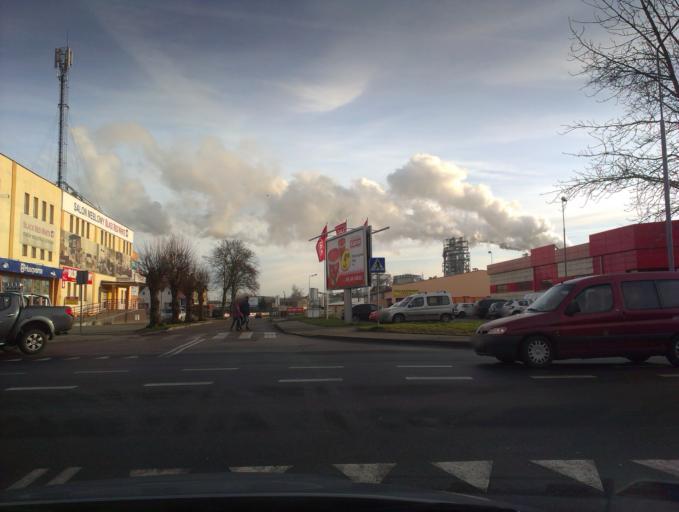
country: PL
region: West Pomeranian Voivodeship
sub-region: Powiat szczecinecki
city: Szczecinek
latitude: 53.6972
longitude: 16.7047
